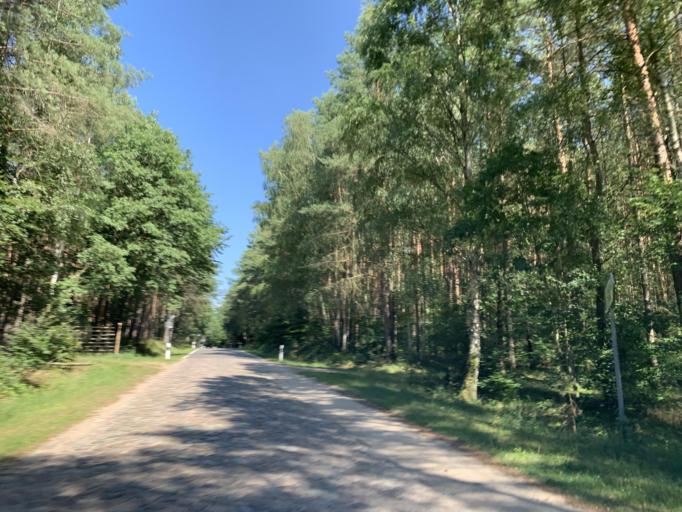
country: DE
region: Mecklenburg-Vorpommern
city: Carpin
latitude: 53.3170
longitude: 13.3235
